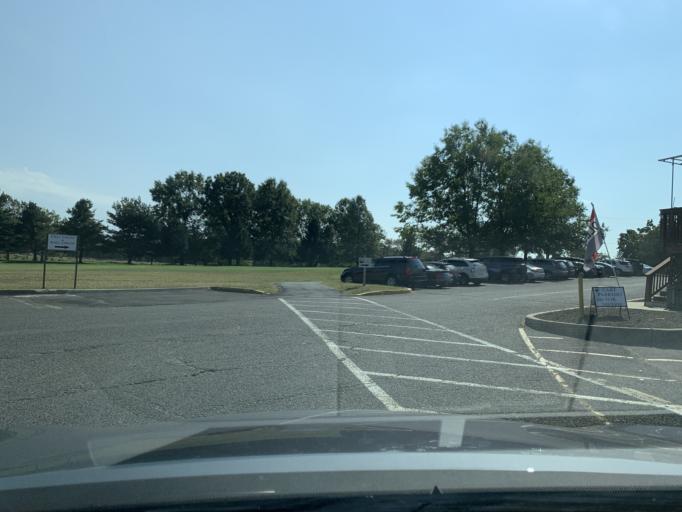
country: US
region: New Jersey
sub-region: Monmouth County
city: Eatontown
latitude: 40.3017
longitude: -74.0717
